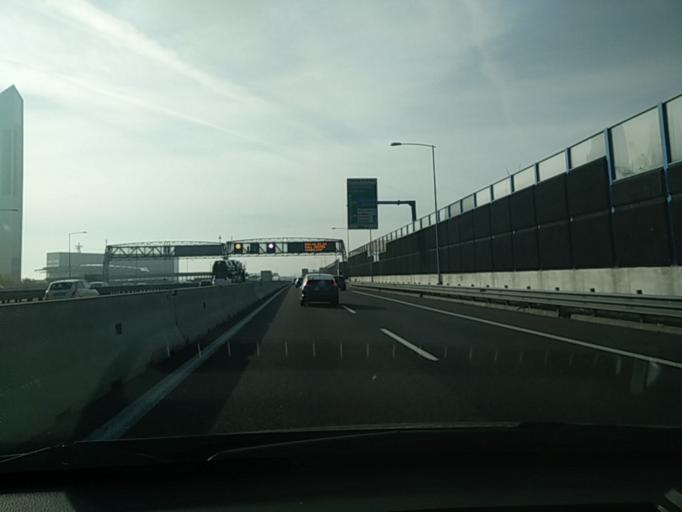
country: IT
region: Emilia-Romagna
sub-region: Provincia di Bologna
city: San Lazzaro
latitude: 44.4980
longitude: 11.3869
